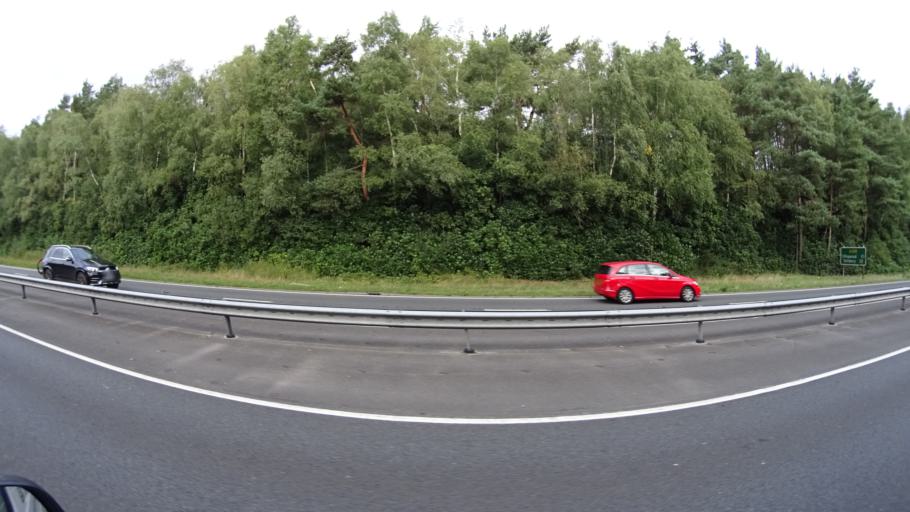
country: GB
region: England
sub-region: Dorset
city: Christchurch
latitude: 50.7684
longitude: -1.8075
